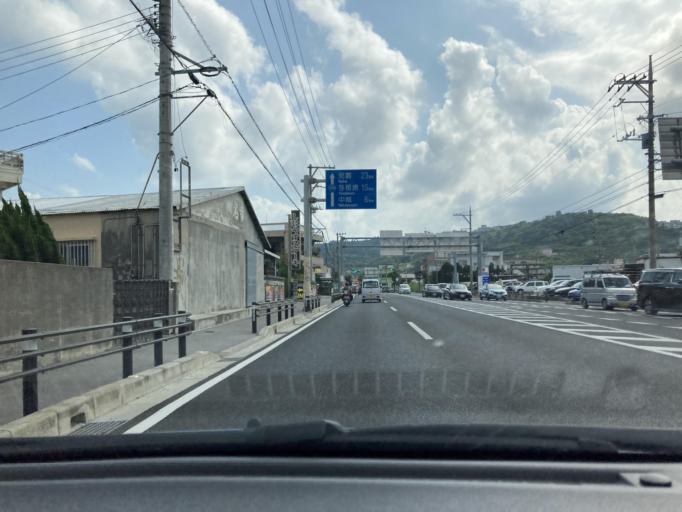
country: JP
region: Okinawa
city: Okinawa
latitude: 26.3018
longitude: 127.8094
